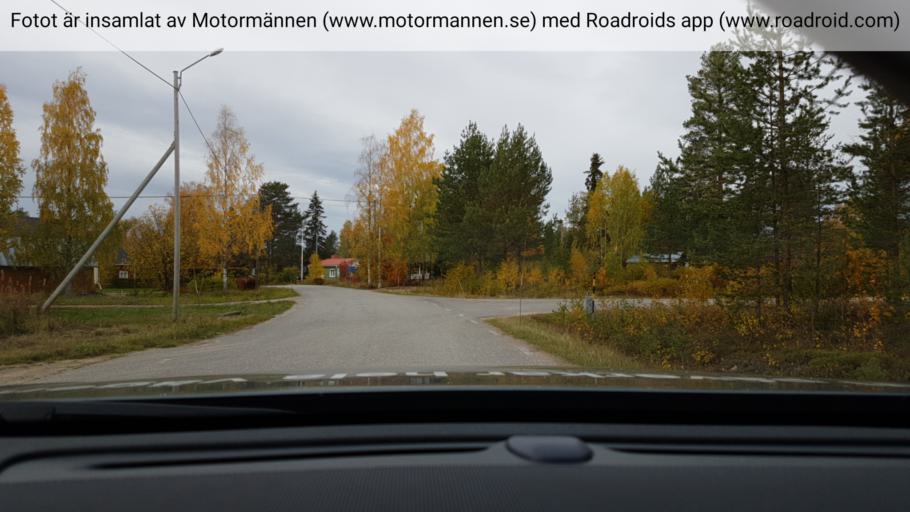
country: SE
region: Norrbotten
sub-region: Overkalix Kommun
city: OEverkalix
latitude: 66.3056
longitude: 22.9216
